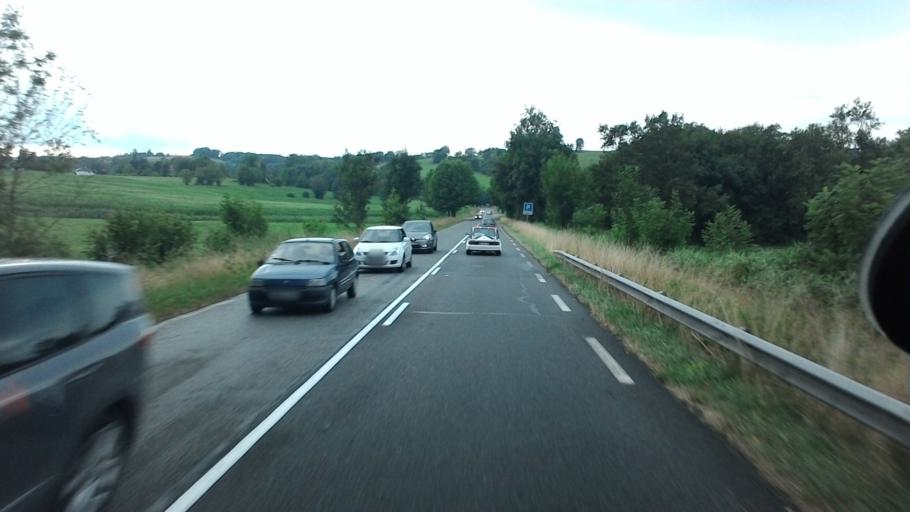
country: FR
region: Rhone-Alpes
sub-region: Departement de la Savoie
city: Yenne
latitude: 45.6940
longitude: 5.8080
